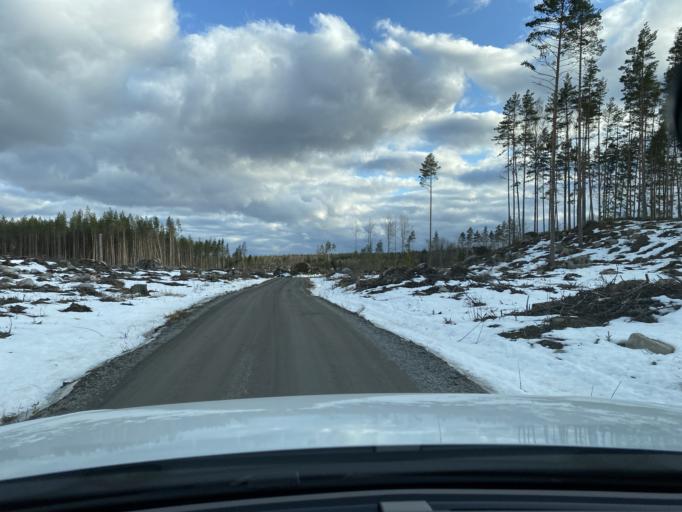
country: FI
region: Pirkanmaa
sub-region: Lounais-Pirkanmaa
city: Mouhijaervi
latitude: 61.4345
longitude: 22.9655
